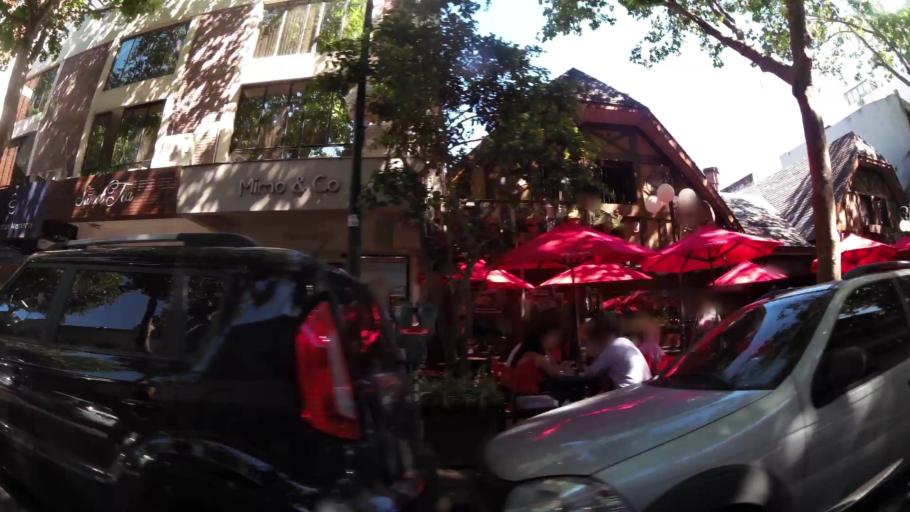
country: AR
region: Buenos Aires
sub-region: Partido de San Isidro
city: San Isidro
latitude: -34.4699
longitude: -58.5108
